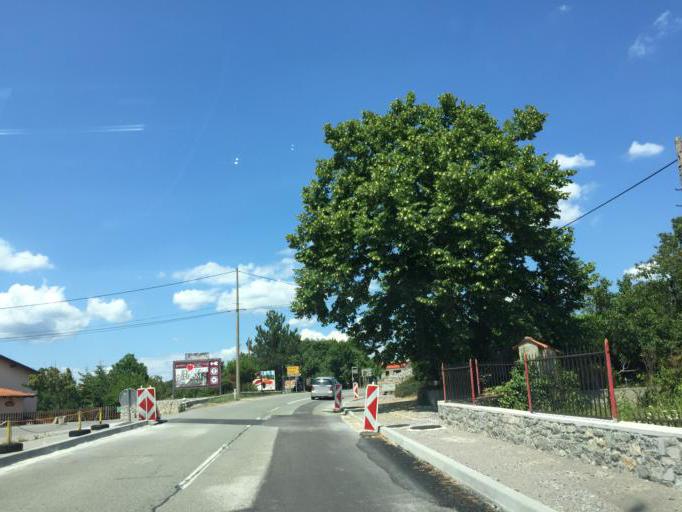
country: SI
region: Sezana
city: Sezana
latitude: 45.7466
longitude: 13.8646
